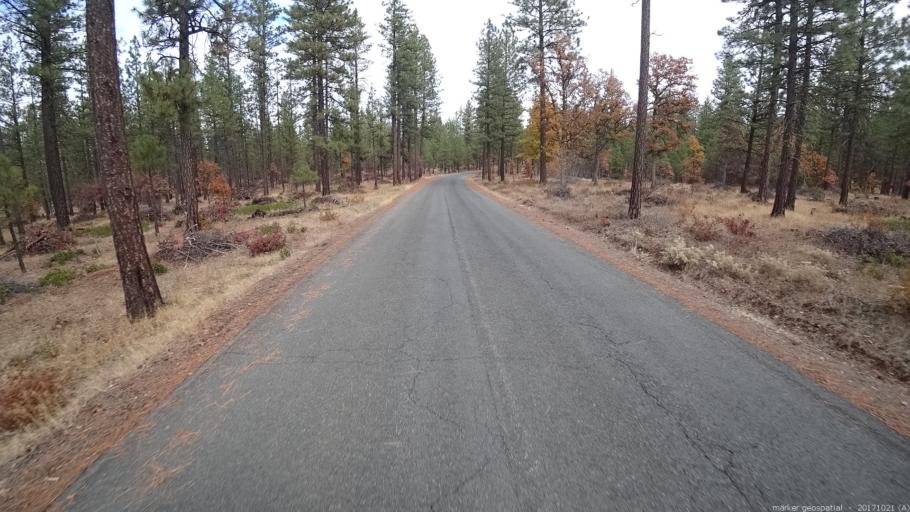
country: US
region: California
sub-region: Shasta County
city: Burney
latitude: 40.9514
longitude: -121.6432
